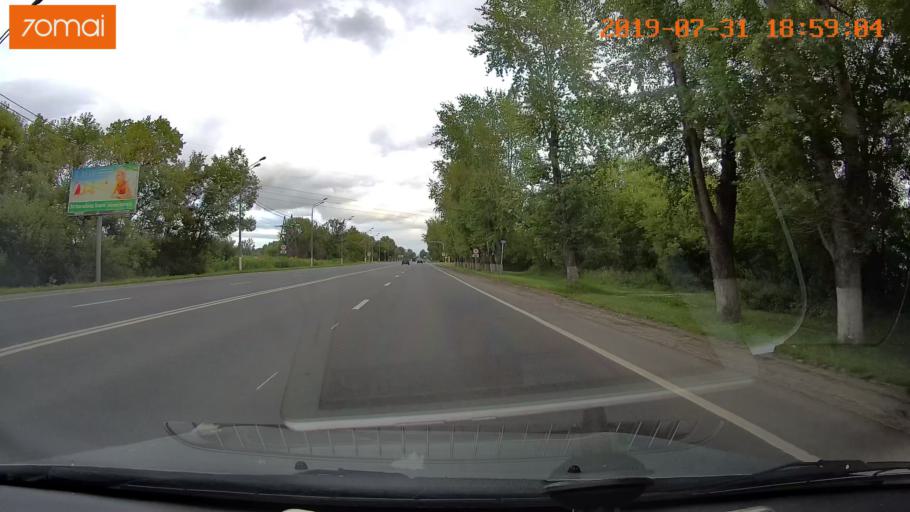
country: RU
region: Moskovskaya
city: Raduzhnyy
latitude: 55.1418
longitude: 38.7117
